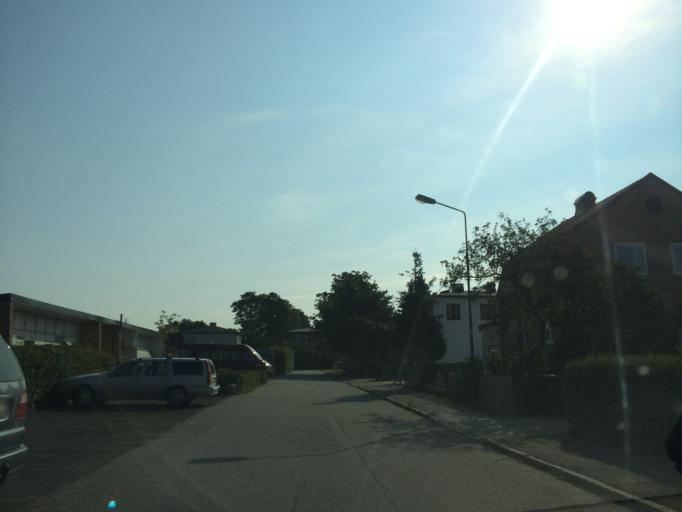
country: SE
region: Skane
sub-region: Burlovs Kommun
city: Arloev
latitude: 55.6355
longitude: 13.0741
